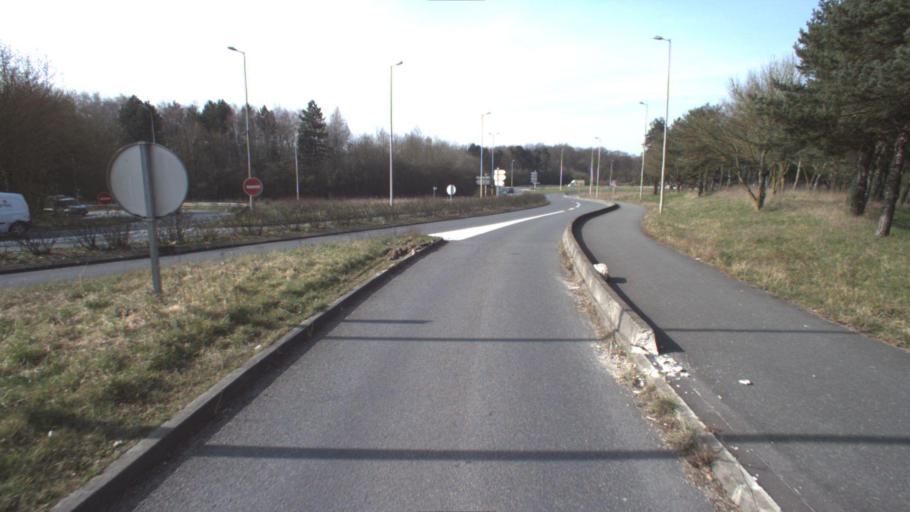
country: FR
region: Ile-de-France
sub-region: Departement de l'Essonne
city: Bondoufle
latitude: 48.6243
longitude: 2.3900
